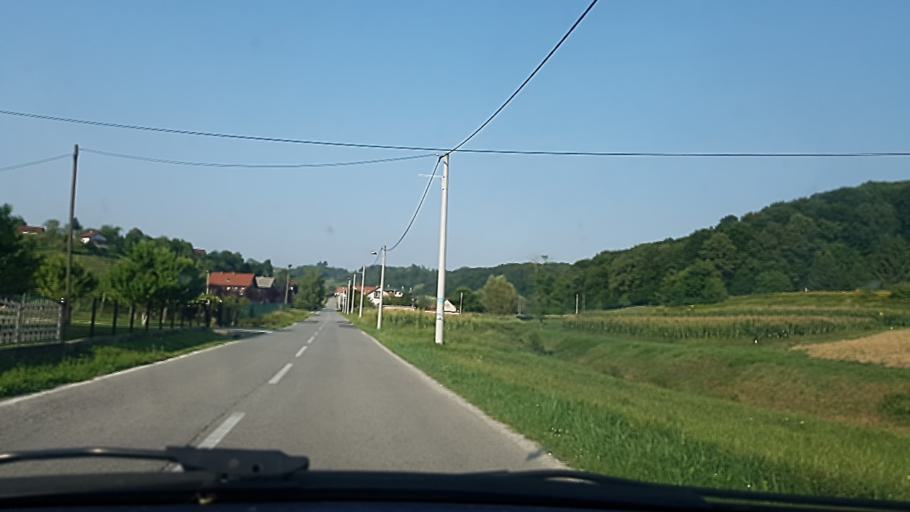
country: HR
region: Zagrebacka
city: Jakovlje
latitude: 45.9621
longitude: 15.8219
